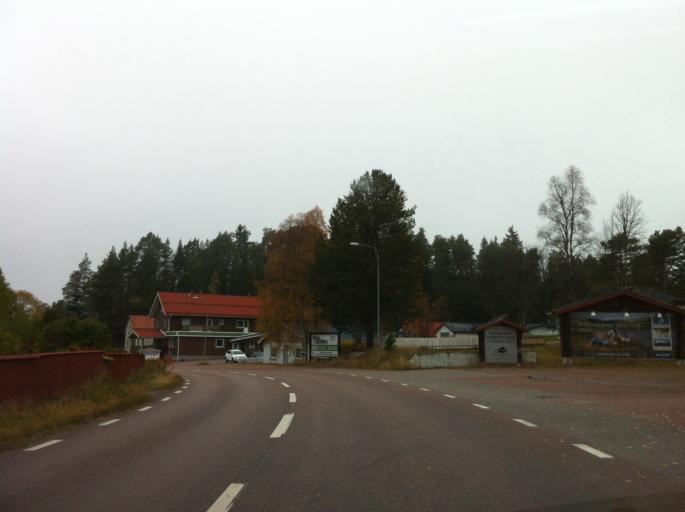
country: NO
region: Hedmark
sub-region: Trysil
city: Innbygda
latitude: 61.8564
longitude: 12.7323
